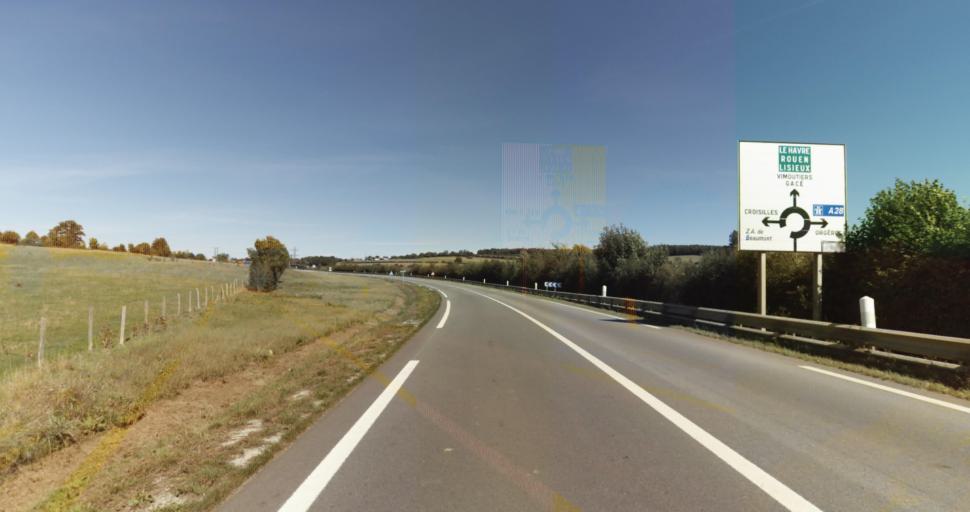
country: FR
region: Lower Normandy
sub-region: Departement de l'Orne
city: Gace
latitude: 48.7747
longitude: 0.2974
